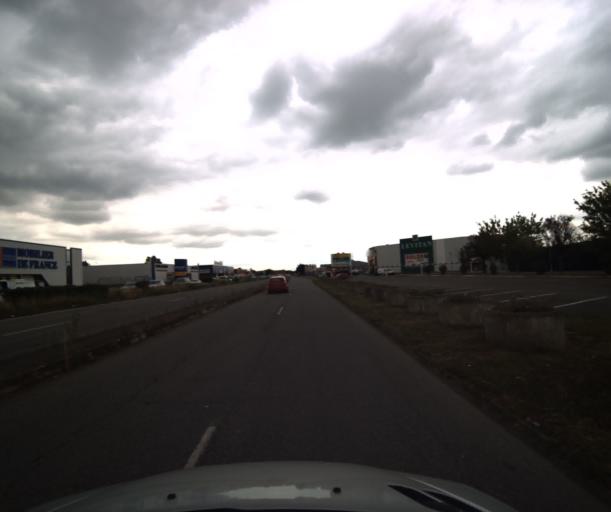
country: FR
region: Midi-Pyrenees
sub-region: Departement de la Haute-Garonne
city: Portet-sur-Garonne
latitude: 43.5294
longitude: 1.4045
